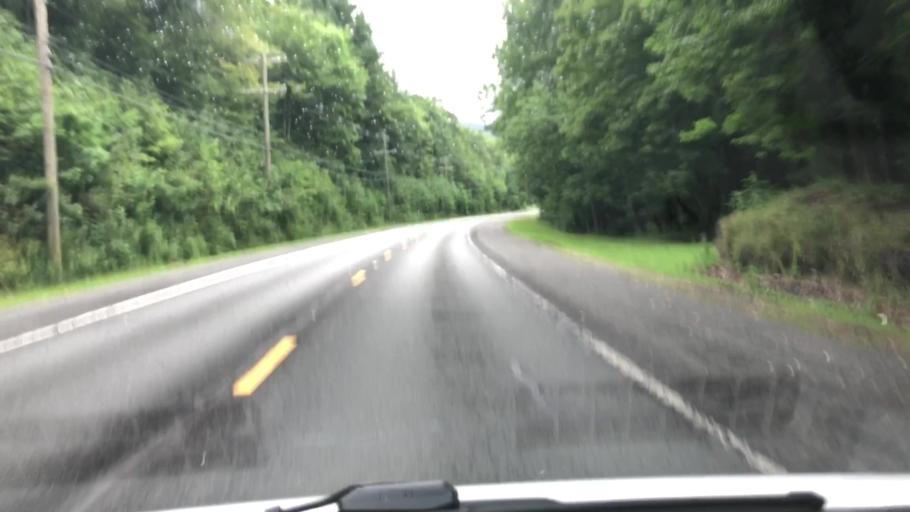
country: US
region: Massachusetts
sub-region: Berkshire County
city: Lanesborough
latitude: 42.5679
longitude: -73.2470
